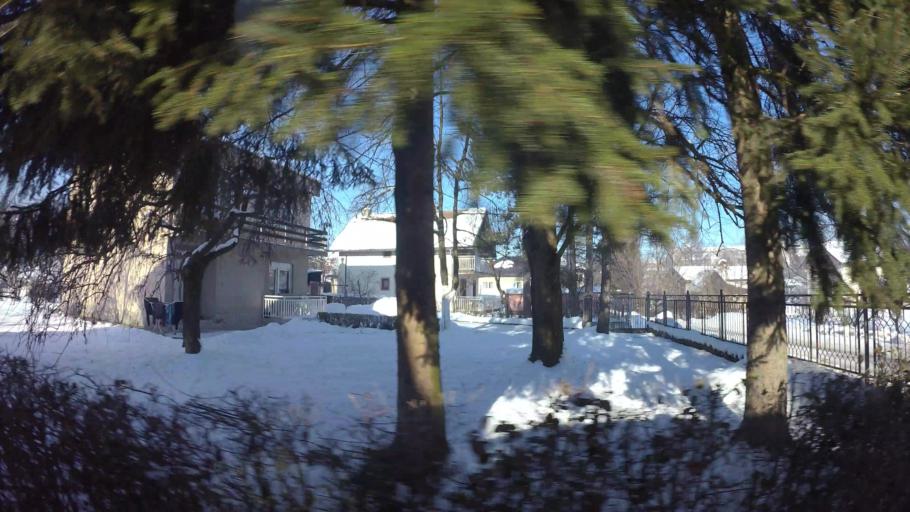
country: BA
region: Federation of Bosnia and Herzegovina
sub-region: Kanton Sarajevo
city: Sarajevo
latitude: 43.8215
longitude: 18.3748
